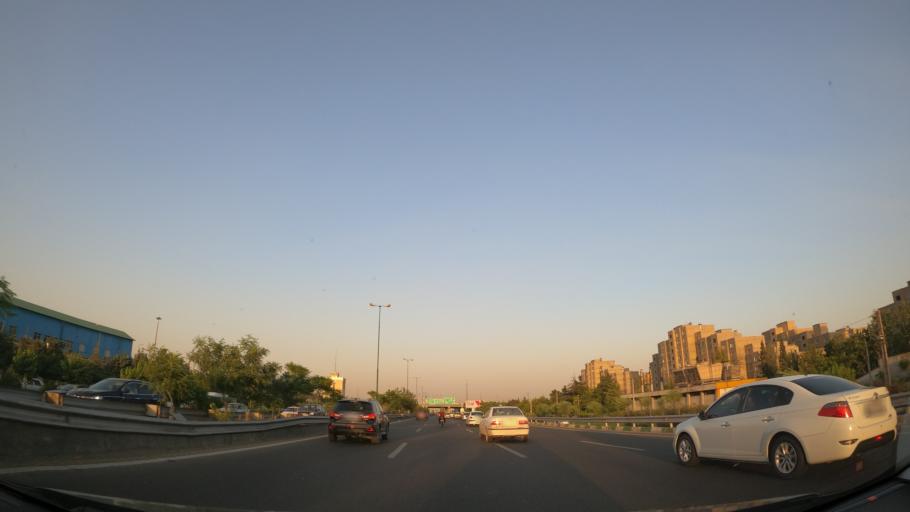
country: IR
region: Tehran
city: Tehran
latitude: 35.7143
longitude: 51.3255
